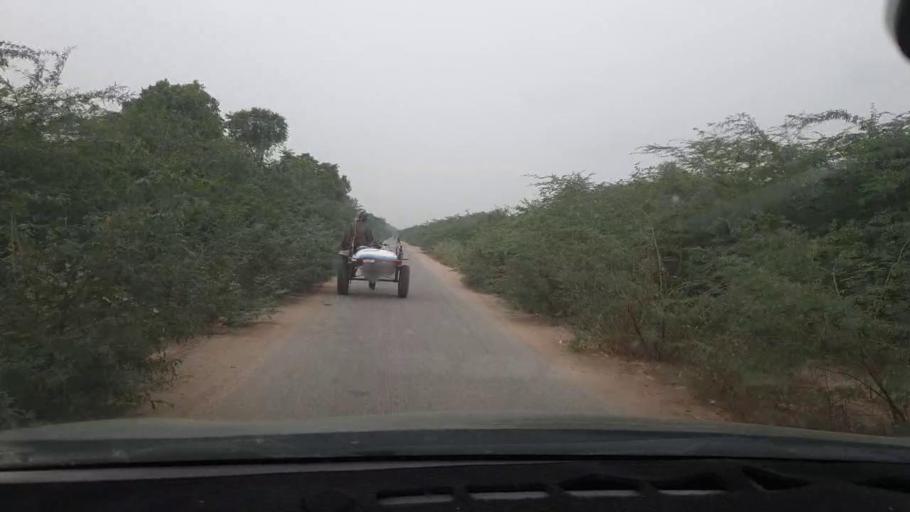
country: PK
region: Sindh
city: Malir Cantonment
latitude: 24.9255
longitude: 67.3254
